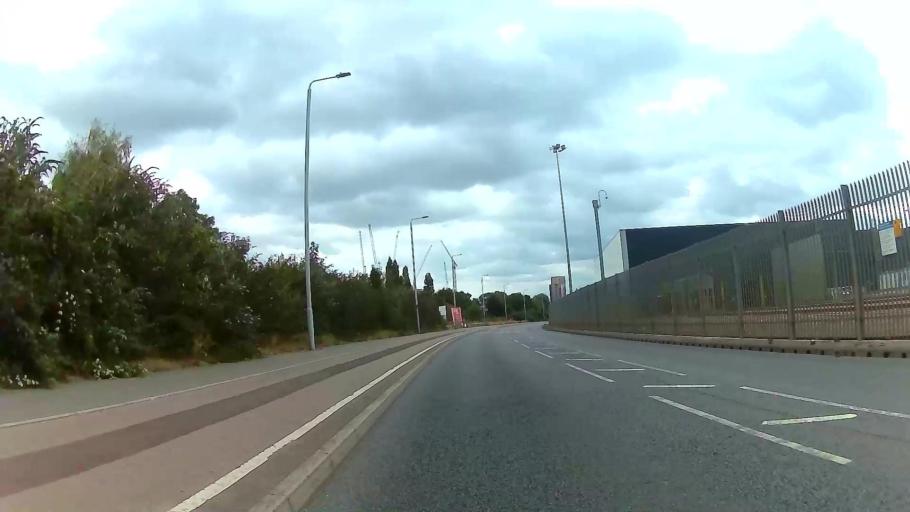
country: GB
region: England
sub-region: Greater London
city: Walthamstow
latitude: 51.5612
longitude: -0.0226
